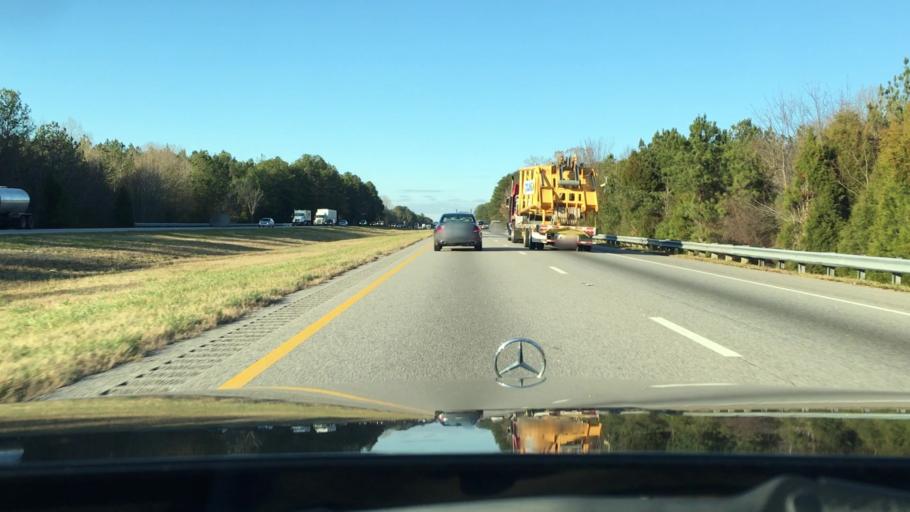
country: US
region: South Carolina
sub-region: Chester County
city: Great Falls
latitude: 34.6703
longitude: -81.0290
